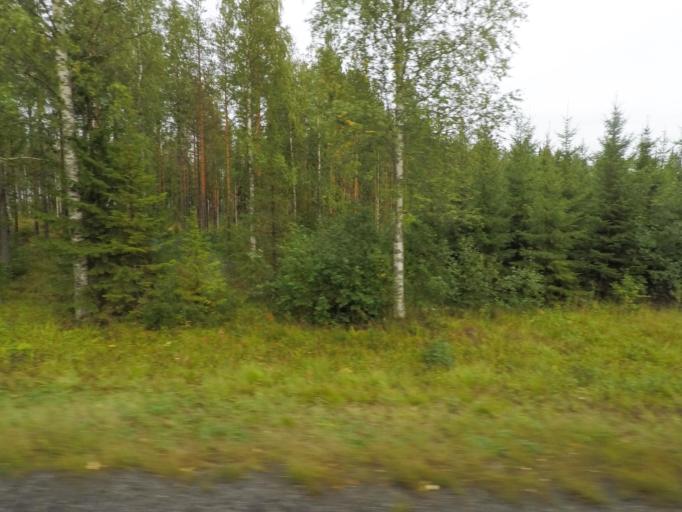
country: FI
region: Southern Savonia
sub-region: Pieksaemaeki
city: Joroinen
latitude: 62.0749
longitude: 27.8177
